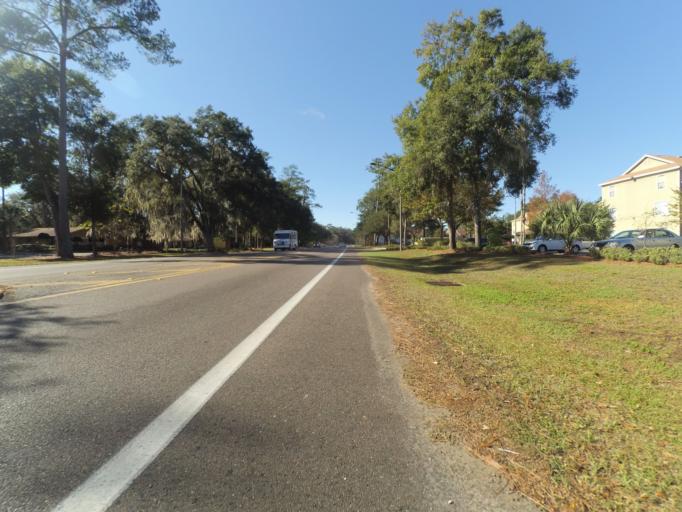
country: US
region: Florida
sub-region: Alachua County
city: Gainesville
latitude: 29.6340
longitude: -82.3792
